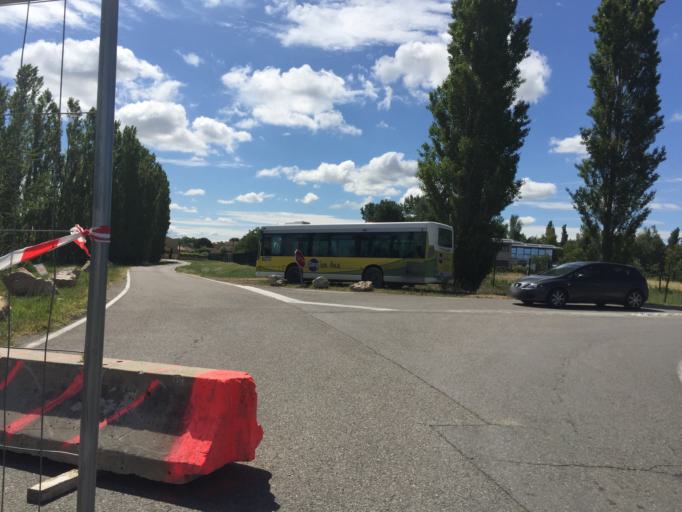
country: FR
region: Provence-Alpes-Cote d'Azur
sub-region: Departement du Vaucluse
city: Vedene
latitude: 43.9919
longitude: 4.8965
